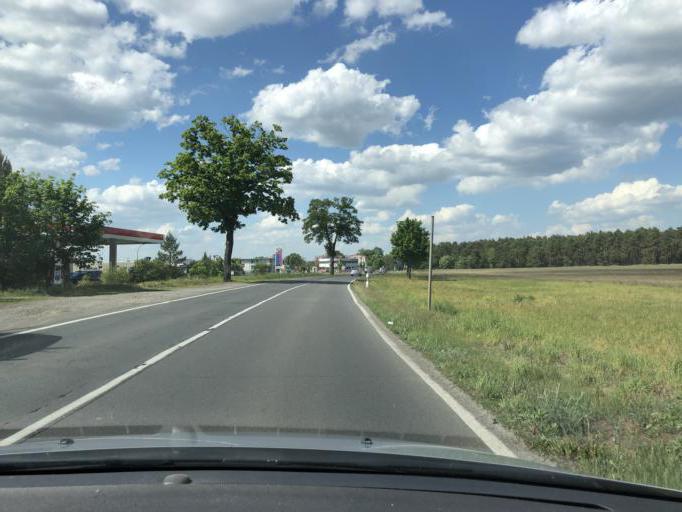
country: DE
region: Brandenburg
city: Spreenhagen
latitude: 52.3241
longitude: 13.9004
